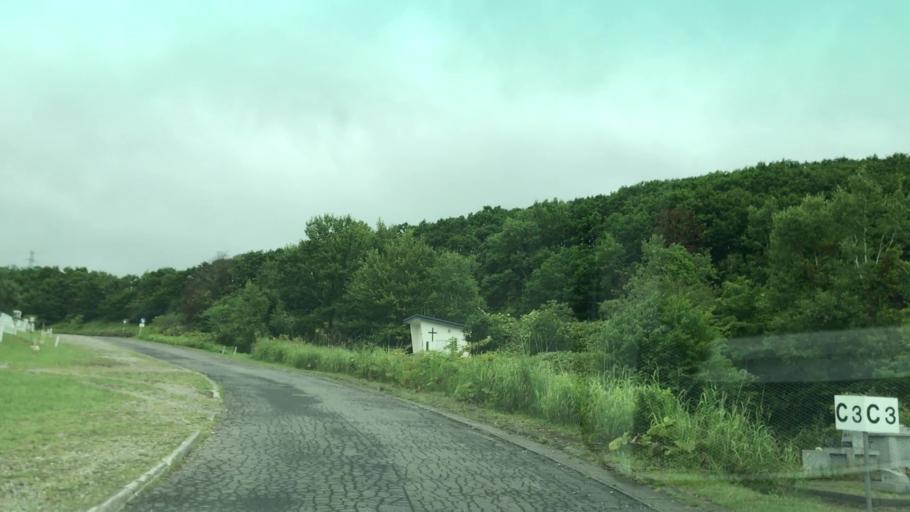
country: JP
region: Hokkaido
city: Muroran
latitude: 42.3953
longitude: 141.0009
